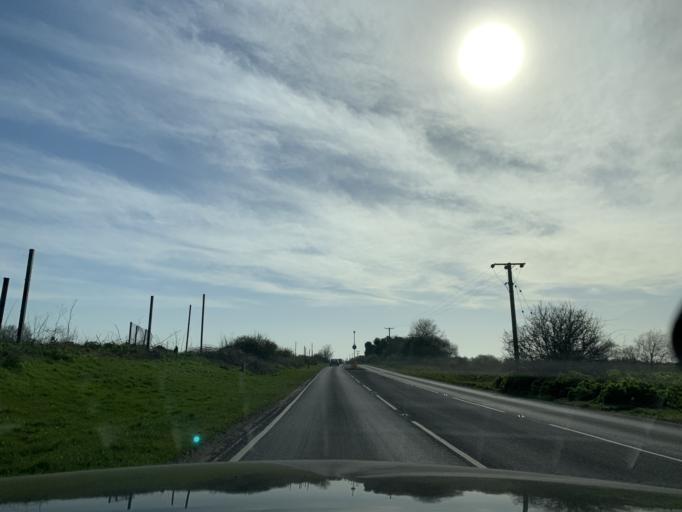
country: GB
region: England
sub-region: Kent
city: Lydd
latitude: 50.9647
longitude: 0.9225
